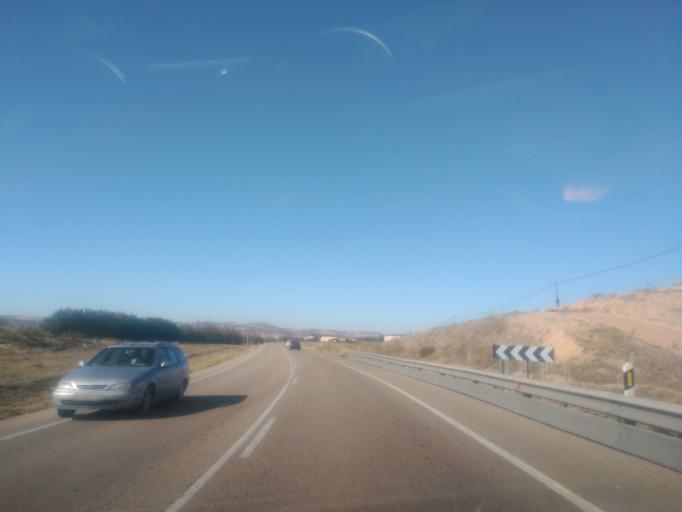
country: ES
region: Castille and Leon
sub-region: Provincia de Valladolid
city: Penafiel
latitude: 41.6082
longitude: -4.1450
